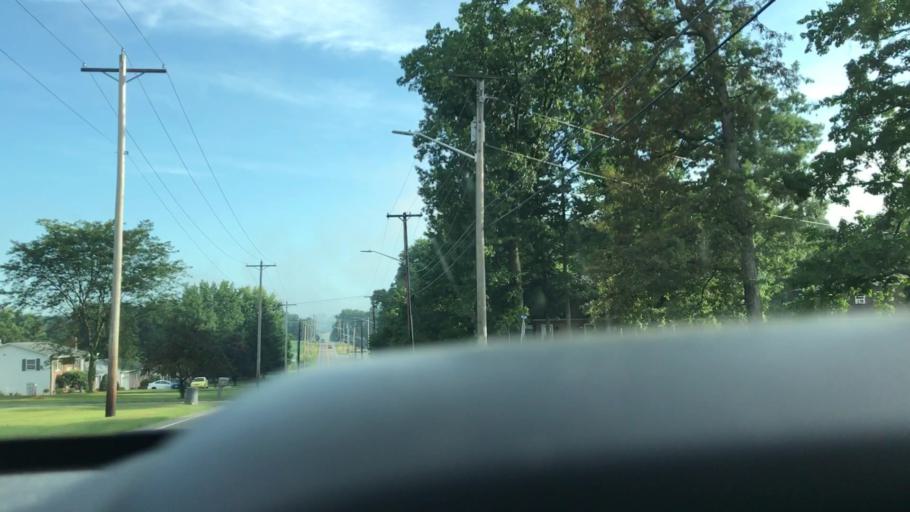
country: US
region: Ohio
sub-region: Stark County
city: Brewster
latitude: 40.7232
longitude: -81.5970
